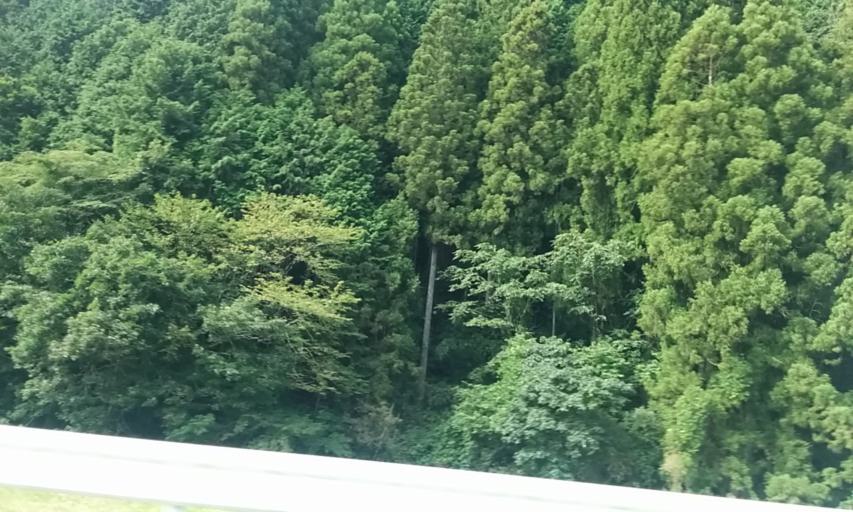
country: JP
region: Gifu
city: Minokamo
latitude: 35.5828
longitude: 137.0845
